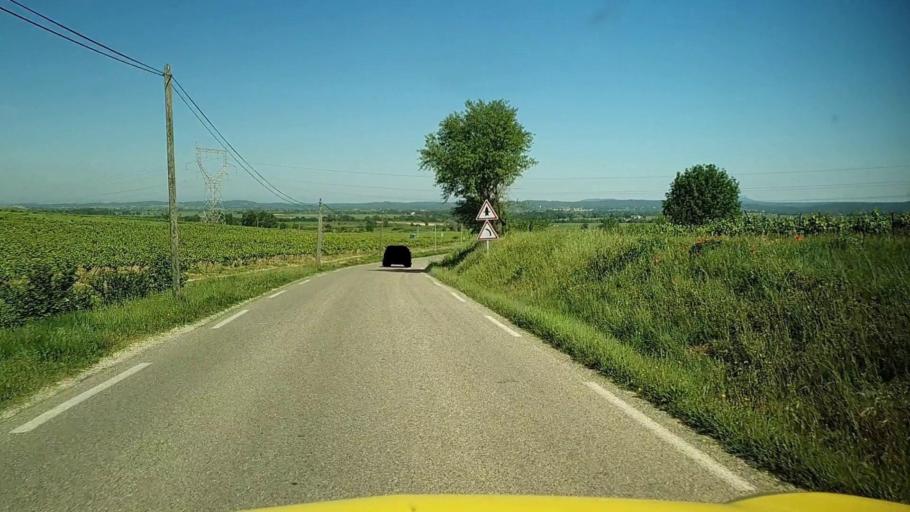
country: FR
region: Languedoc-Roussillon
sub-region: Departement du Gard
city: Blauzac
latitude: 43.9463
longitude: 4.3468
